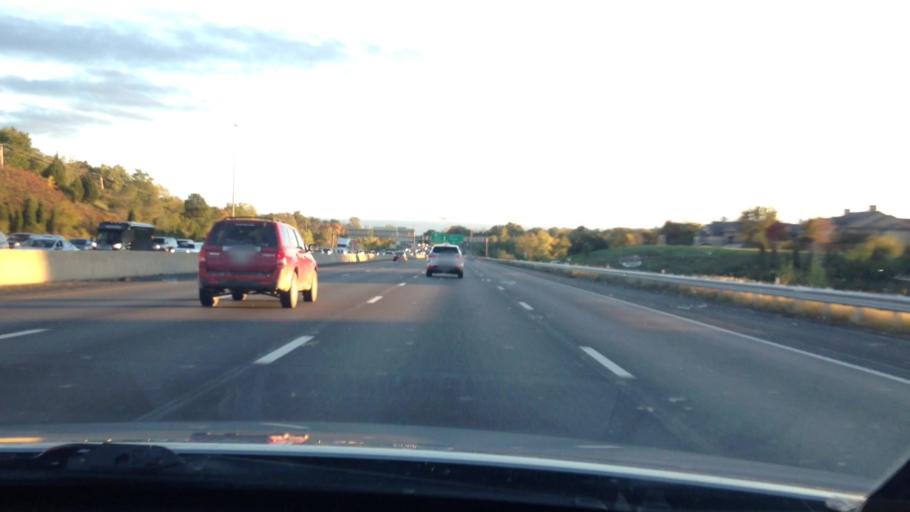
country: US
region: Missouri
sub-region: Jackson County
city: Raytown
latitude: 39.0303
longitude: -94.5007
